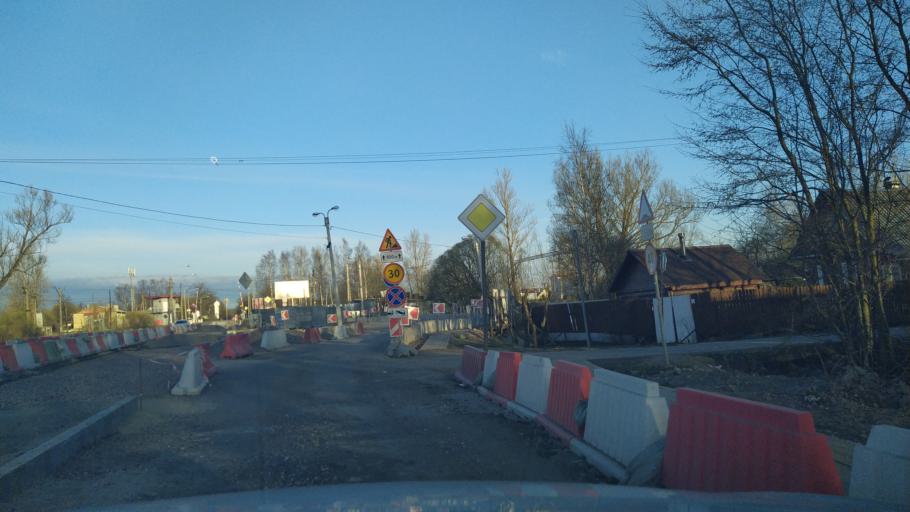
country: RU
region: St.-Petersburg
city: Aleksandrovskaya
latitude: 59.7339
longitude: 30.3393
